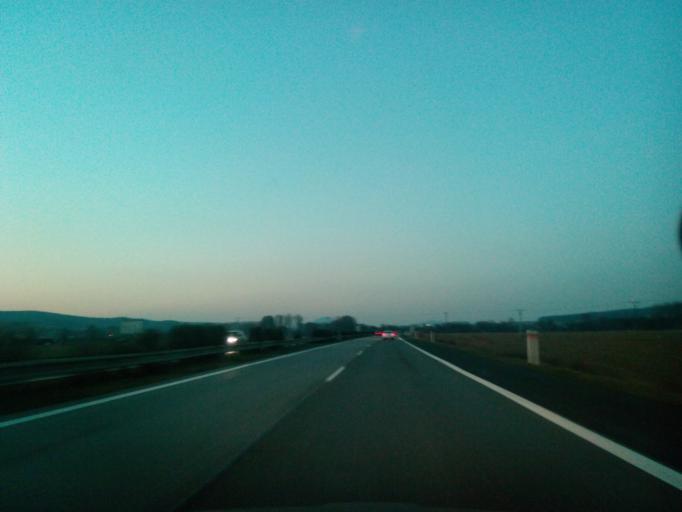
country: SK
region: Presovsky
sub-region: Okres Presov
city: Presov
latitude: 48.9052
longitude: 21.2496
